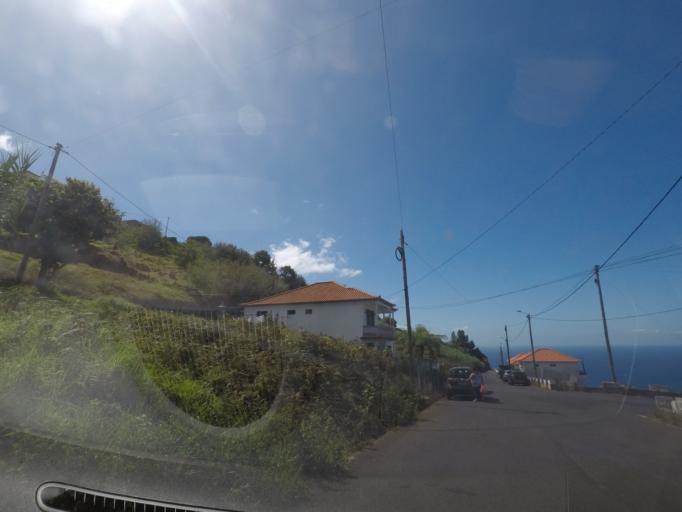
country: PT
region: Madeira
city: Ponta do Sol
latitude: 32.6930
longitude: -17.0876
